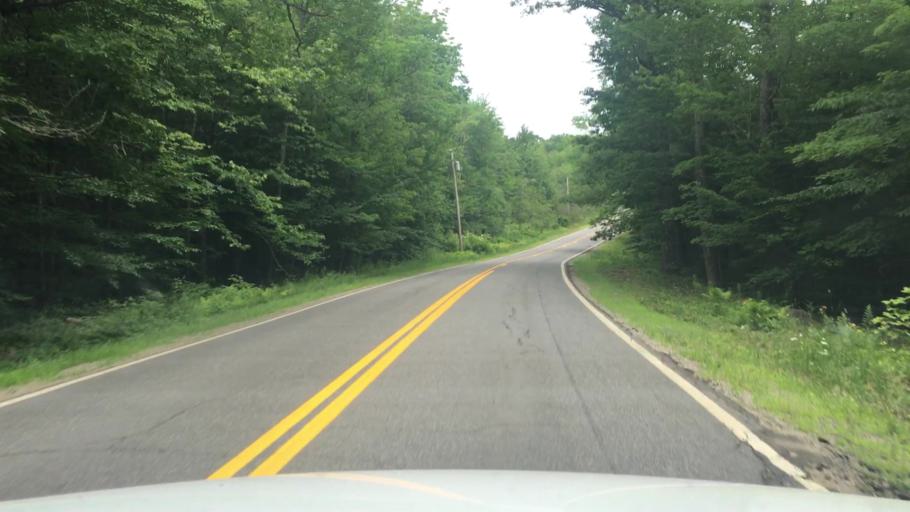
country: US
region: Maine
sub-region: Waldo County
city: Searsmont
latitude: 44.4524
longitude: -69.2777
